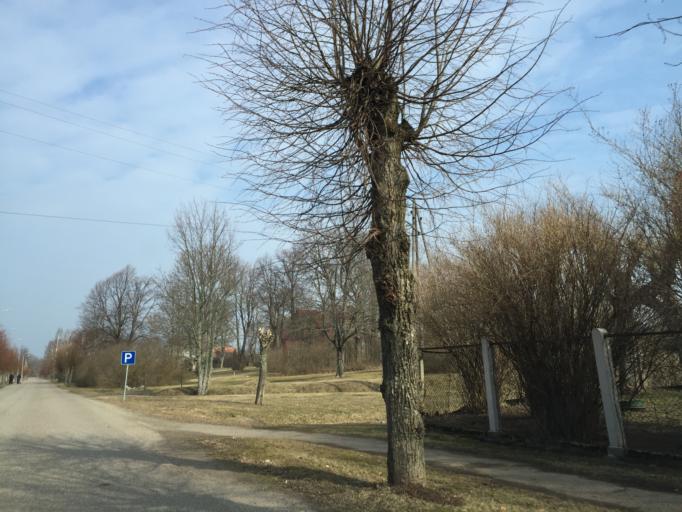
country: LV
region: Salacgrivas
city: Ainazi
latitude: 57.8660
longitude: 24.3594
